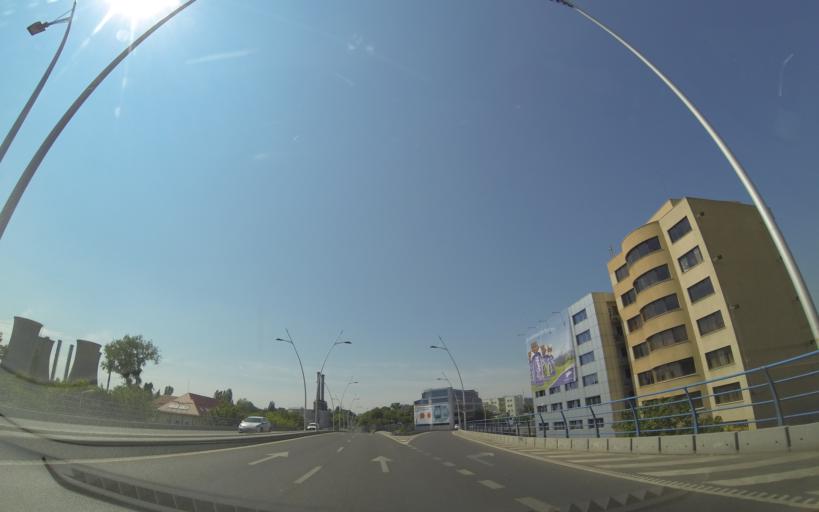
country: RO
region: Bucuresti
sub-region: Municipiul Bucuresti
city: Bucuresti
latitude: 44.4422
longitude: 26.0603
